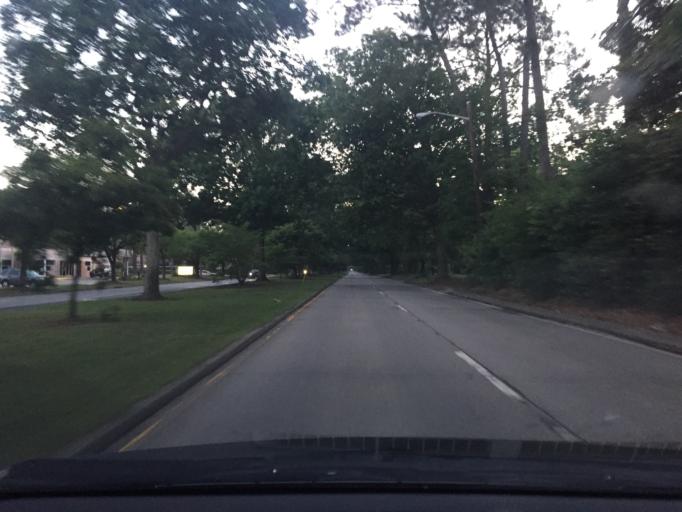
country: US
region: Georgia
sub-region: Chatham County
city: Savannah
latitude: 32.0292
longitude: -81.1078
